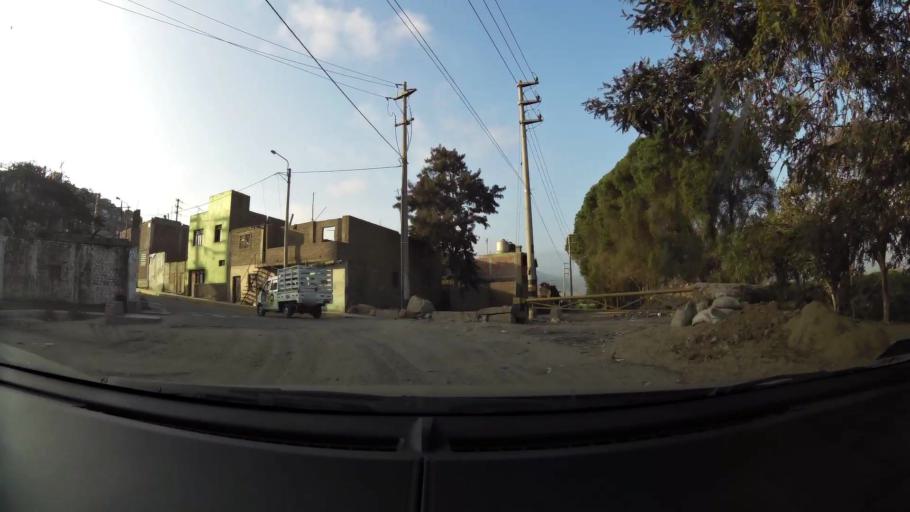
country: PE
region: La Libertad
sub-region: Provincia de Trujillo
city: El Porvenir
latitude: -8.0888
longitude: -78.9919
